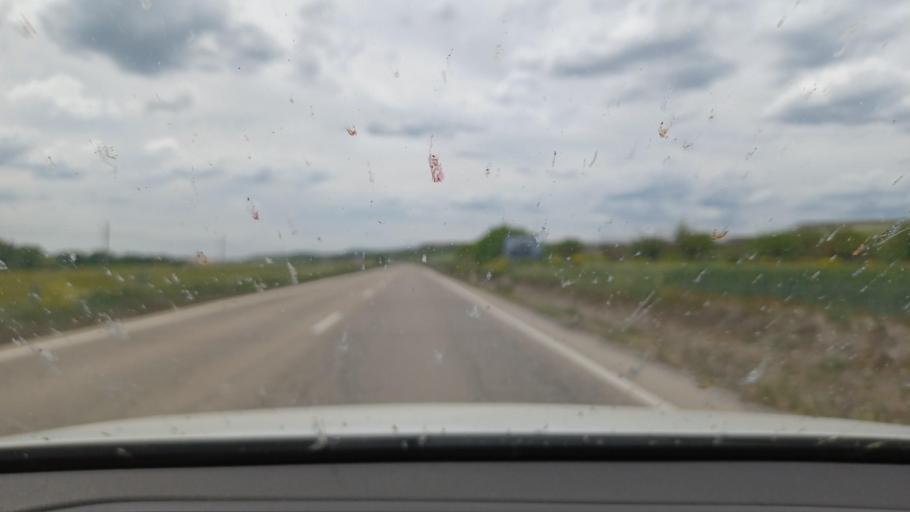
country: ES
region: Castille and Leon
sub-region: Provincia de Segovia
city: Cuellar
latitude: 41.3871
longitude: -4.2740
